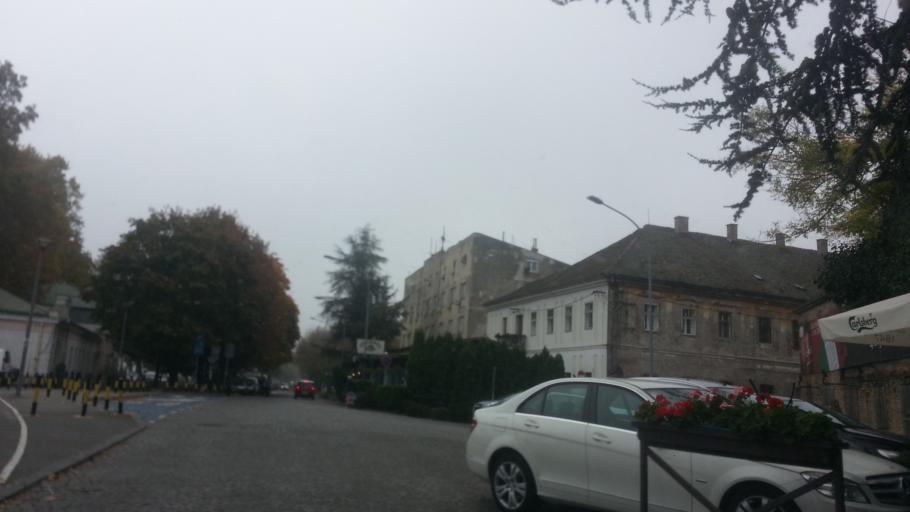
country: RS
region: Central Serbia
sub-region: Belgrade
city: Zemun
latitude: 44.8471
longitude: 20.4143
